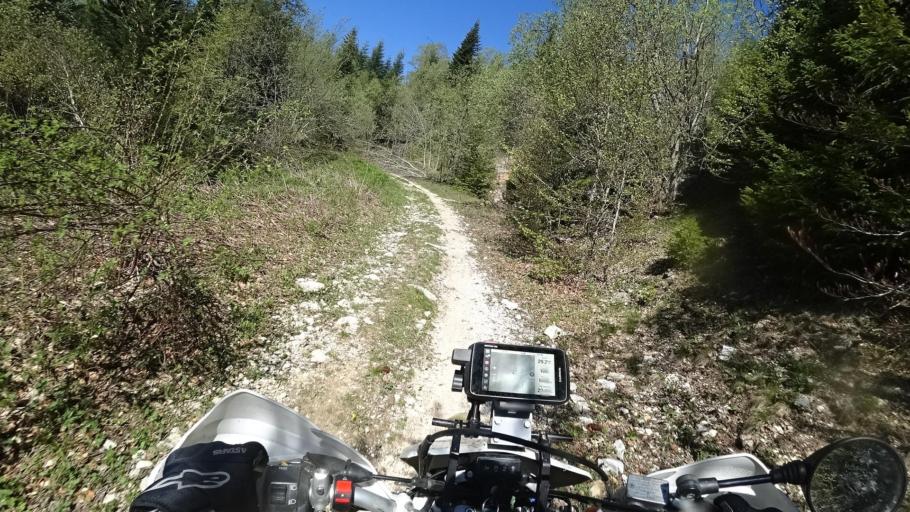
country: BA
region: Federation of Bosnia and Herzegovina
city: Rumboci
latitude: 43.8687
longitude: 17.4831
